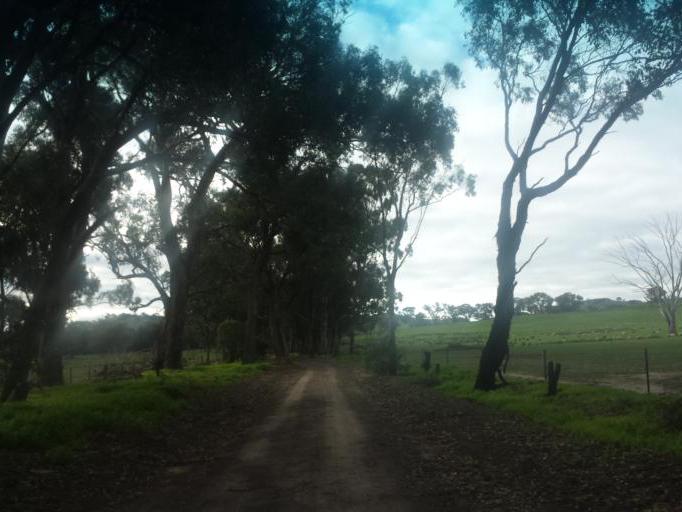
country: AU
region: Victoria
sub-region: Murrindindi
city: Kinglake West
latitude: -37.0192
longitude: 145.2502
